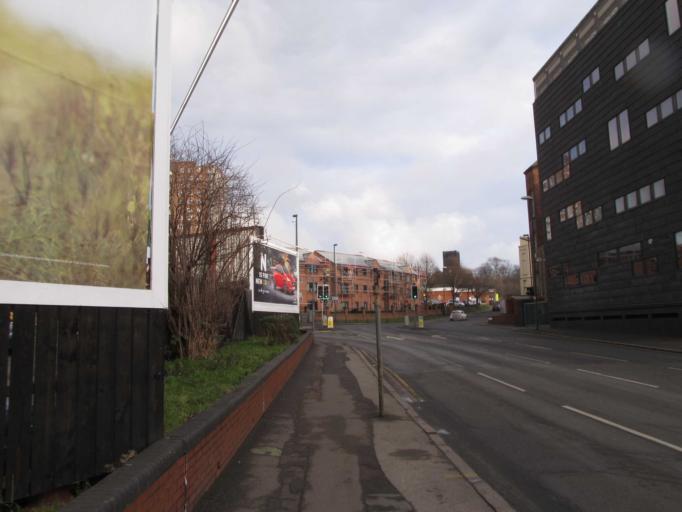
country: GB
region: England
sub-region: Nottingham
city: Nottingham
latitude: 52.9514
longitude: -1.1366
